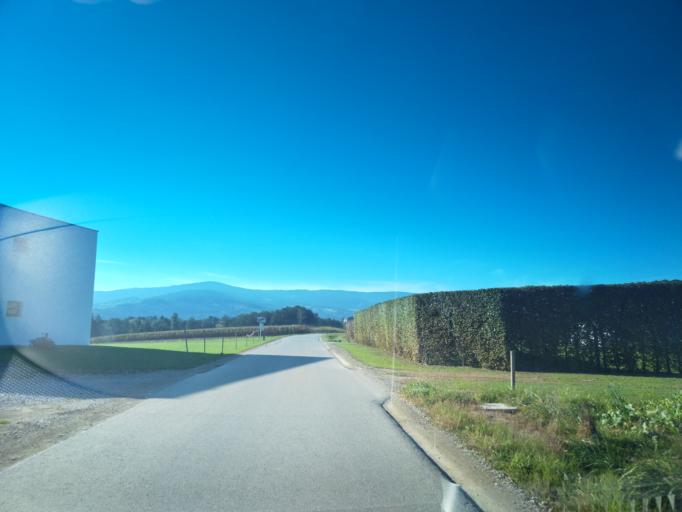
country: AT
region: Styria
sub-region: Politischer Bezirk Deutschlandsberg
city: Stallhof
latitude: 46.8889
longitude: 15.2945
